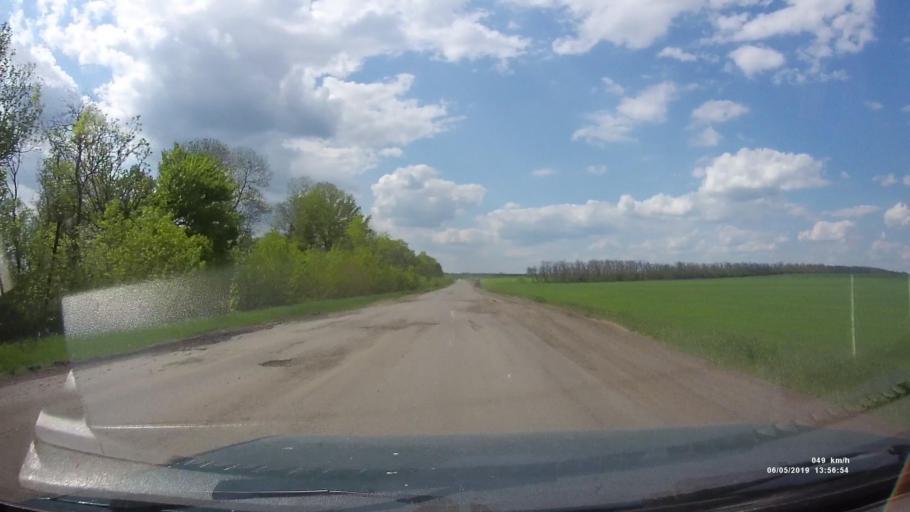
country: RU
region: Rostov
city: Melikhovskaya
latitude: 47.6828
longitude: 40.4269
